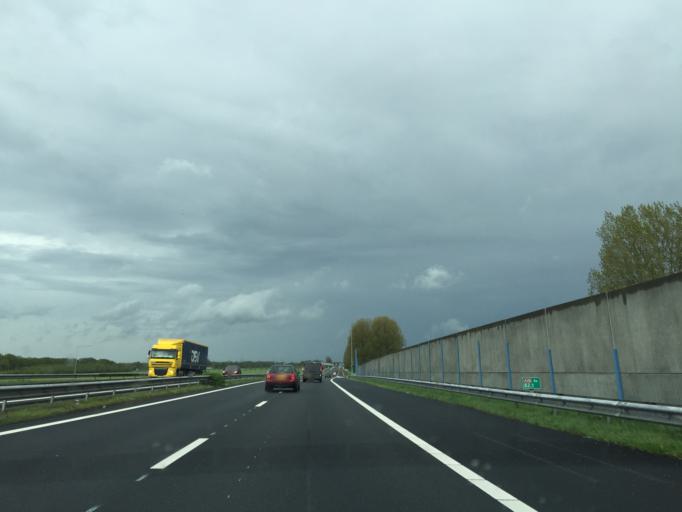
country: NL
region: Gelderland
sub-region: Gemeente Hattem
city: Hattem
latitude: 52.4675
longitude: 5.9886
